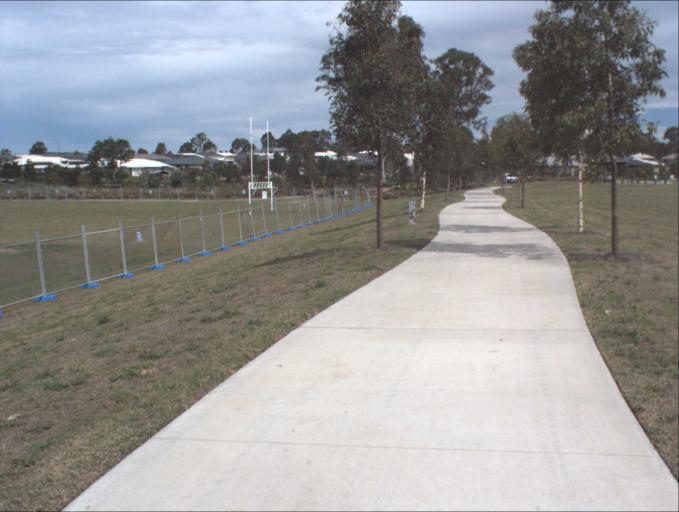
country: AU
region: Queensland
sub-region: Logan
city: Waterford West
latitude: -27.7095
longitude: 153.1135
